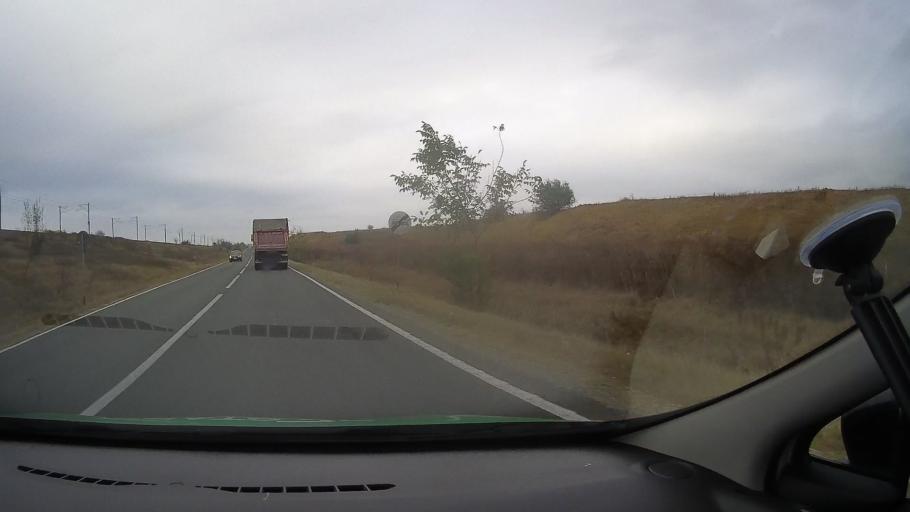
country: RO
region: Constanta
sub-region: Comuna Poarta Alba
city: Poarta Alba
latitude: 44.2224
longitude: 28.3865
